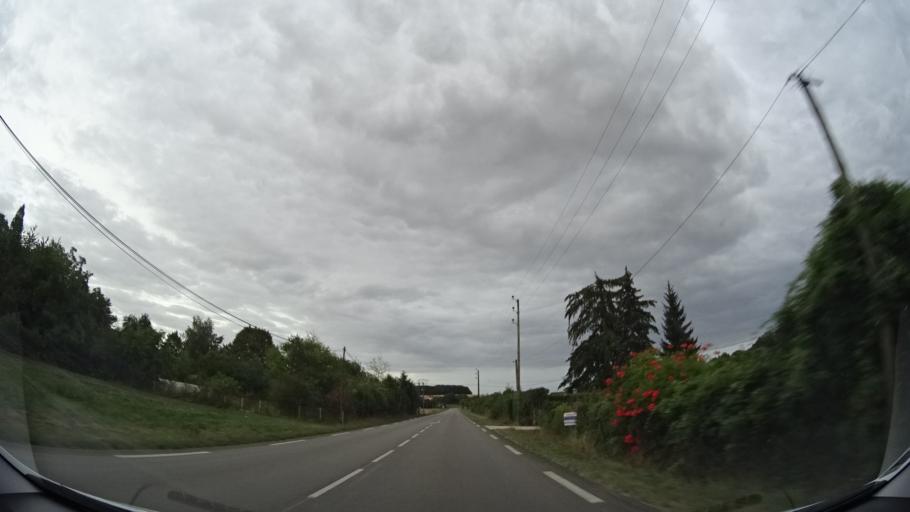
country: FR
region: Centre
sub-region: Departement du Loiret
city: Douchy
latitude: 47.9353
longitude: 3.0854
